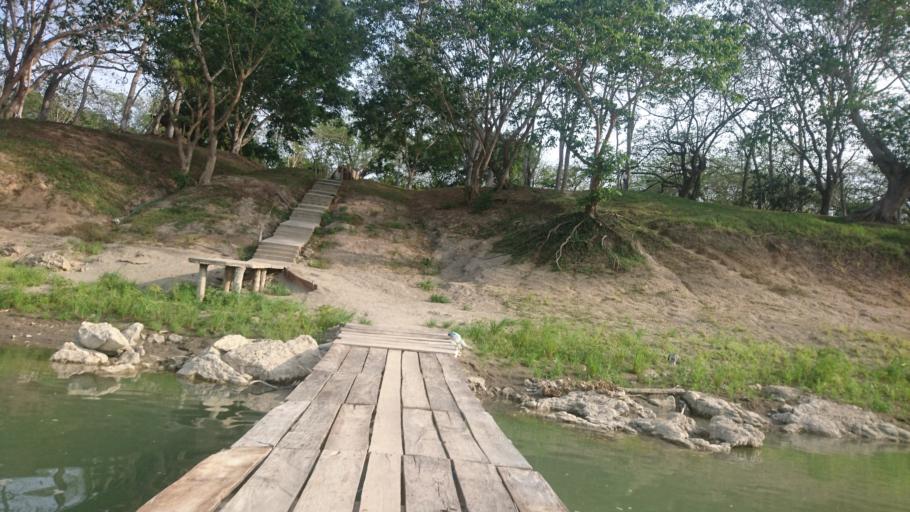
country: MX
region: Chiapas
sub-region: Ocosingo
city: Frontera Corozal
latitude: 16.8238
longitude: -90.8855
